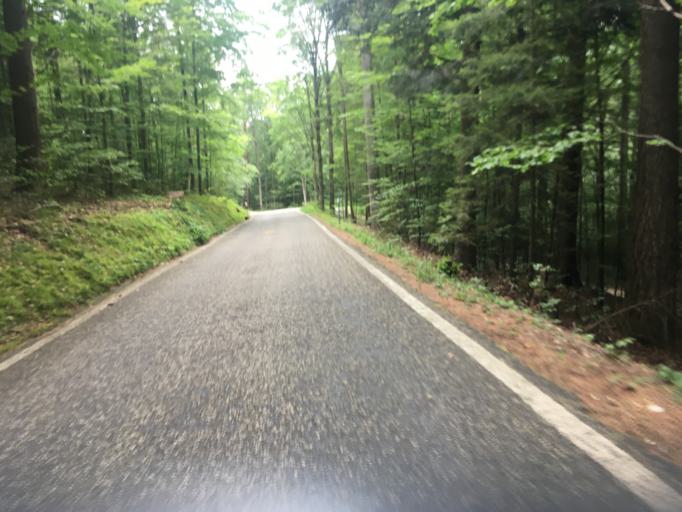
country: CH
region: Solothurn
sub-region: Bezirk Thal
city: Welschenrohr
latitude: 47.2597
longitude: 7.4924
